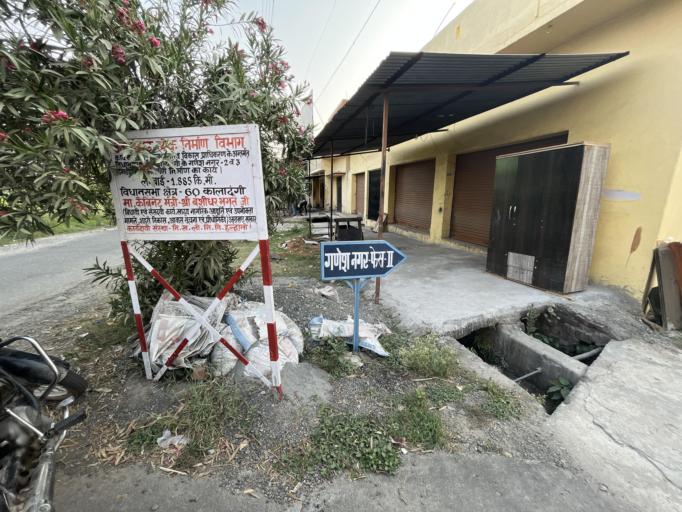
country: IN
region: Uttarakhand
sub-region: Naini Tal
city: Haldwani
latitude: 29.2348
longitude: 79.4727
